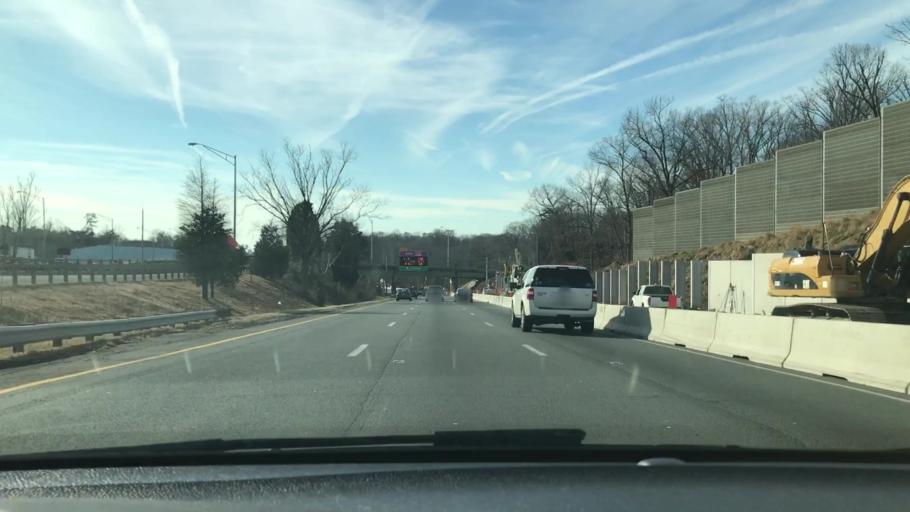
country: US
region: Virginia
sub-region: Fairfax County
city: Lincolnia
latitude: 38.8129
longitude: -77.1465
